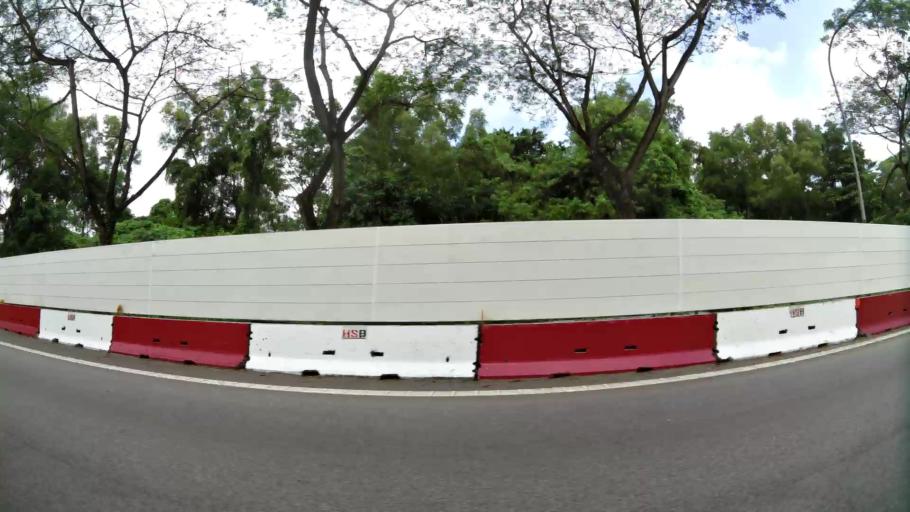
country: MY
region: Johor
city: Kampung Pasir Gudang Baru
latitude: 1.3767
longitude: 103.9105
